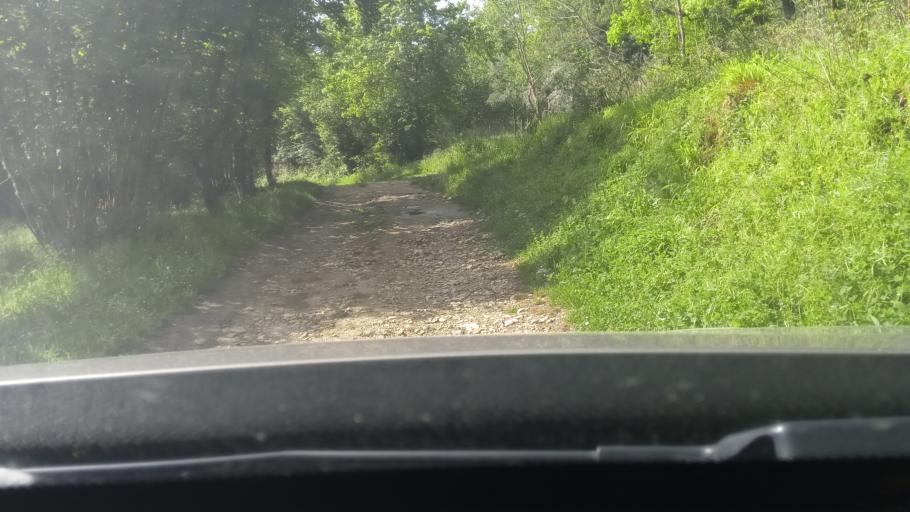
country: IT
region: Latium
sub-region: Provincia di Latina
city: Minturno
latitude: 41.2813
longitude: 13.7634
